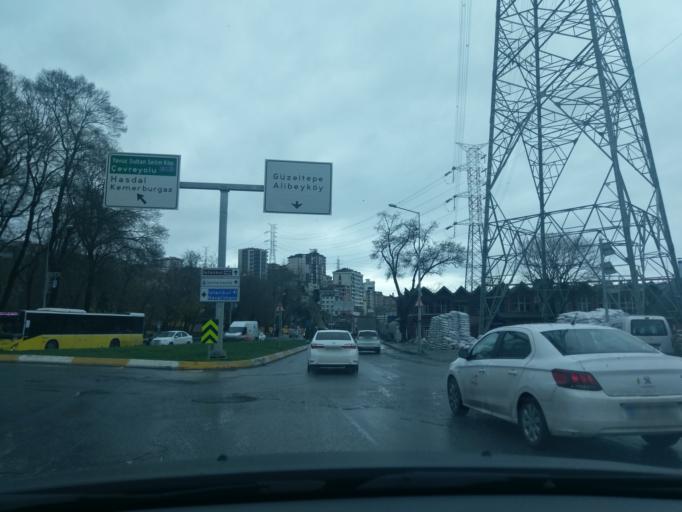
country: TR
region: Istanbul
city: Sisli
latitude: 41.0853
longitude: 28.9517
